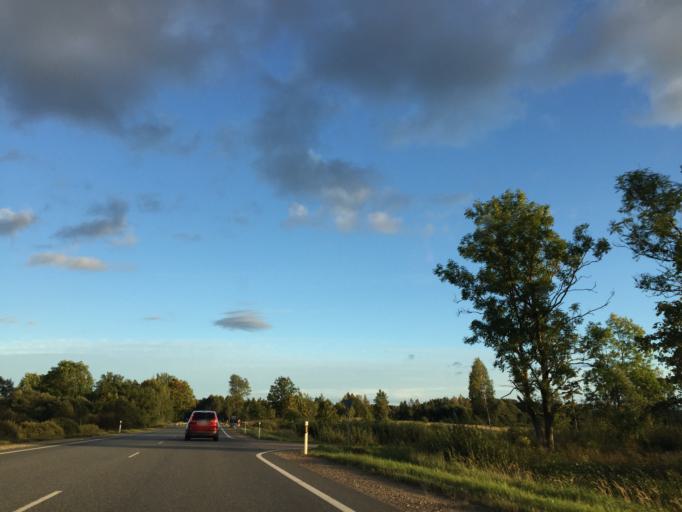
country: LV
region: Broceni
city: Broceni
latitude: 56.6727
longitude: 22.5868
